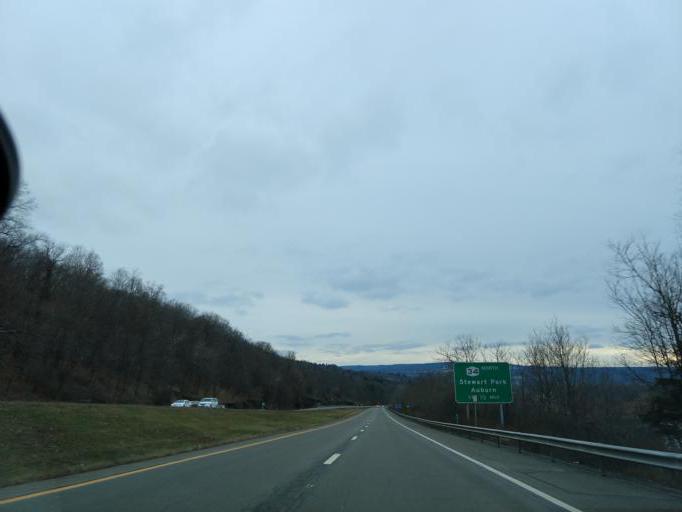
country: US
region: New York
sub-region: Tompkins County
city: Cayuga Heights
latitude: 42.4696
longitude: -76.5001
